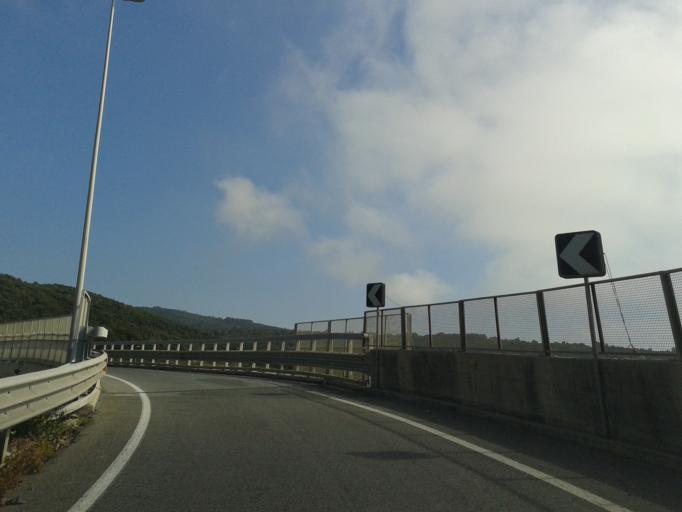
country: IT
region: Tuscany
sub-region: Provincia di Livorno
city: Quercianella
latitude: 43.4838
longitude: 10.3337
